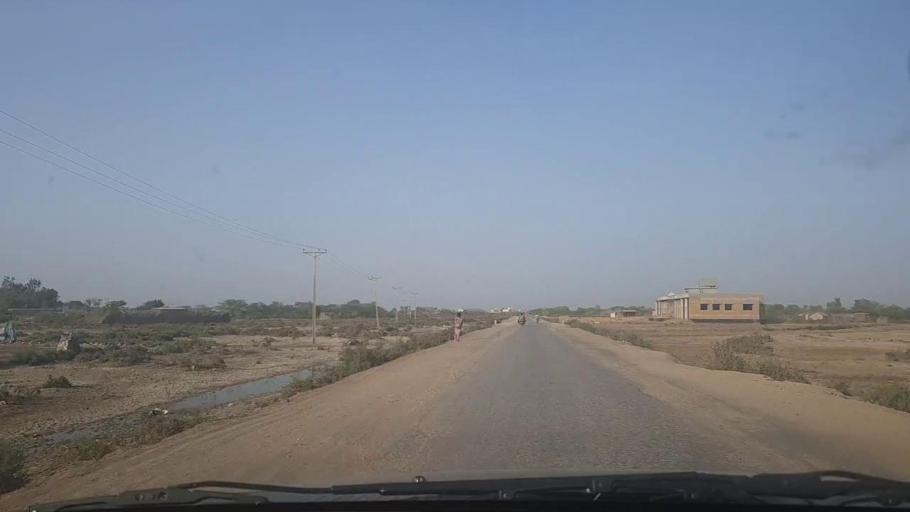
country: PK
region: Sindh
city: Keti Bandar
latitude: 24.3064
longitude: 67.6058
